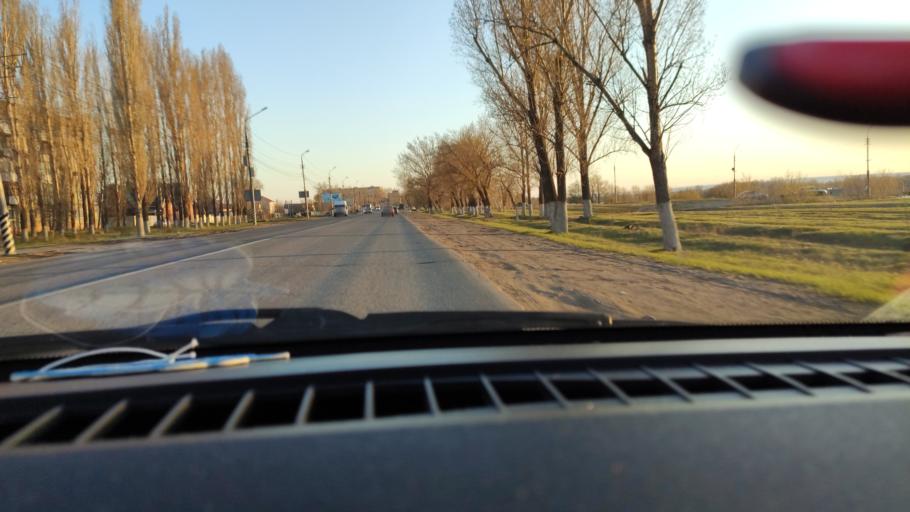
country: RU
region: Saratov
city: Engel's
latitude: 51.4506
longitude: 46.0821
